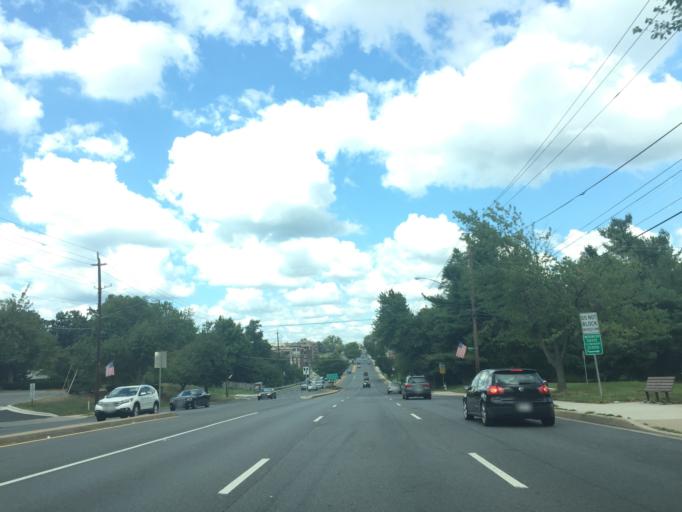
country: US
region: Maryland
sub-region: Montgomery County
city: Gaithersburg
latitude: 39.1299
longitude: -77.1868
